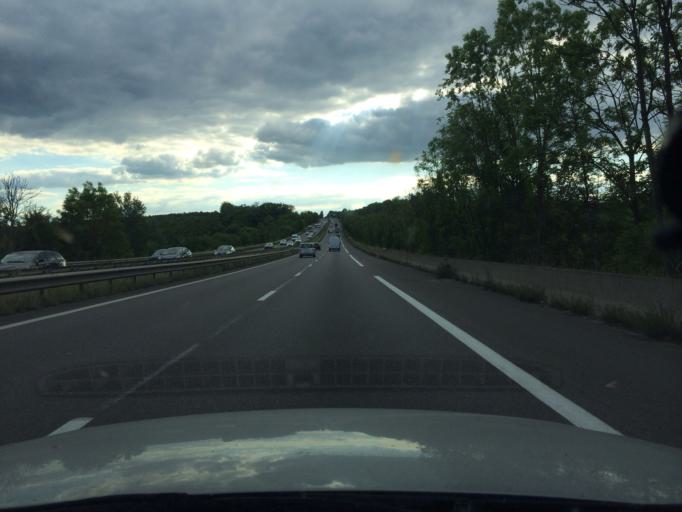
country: FR
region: Lorraine
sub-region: Departement de Meurthe-et-Moselle
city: Laxou
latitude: 48.6941
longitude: 6.0907
